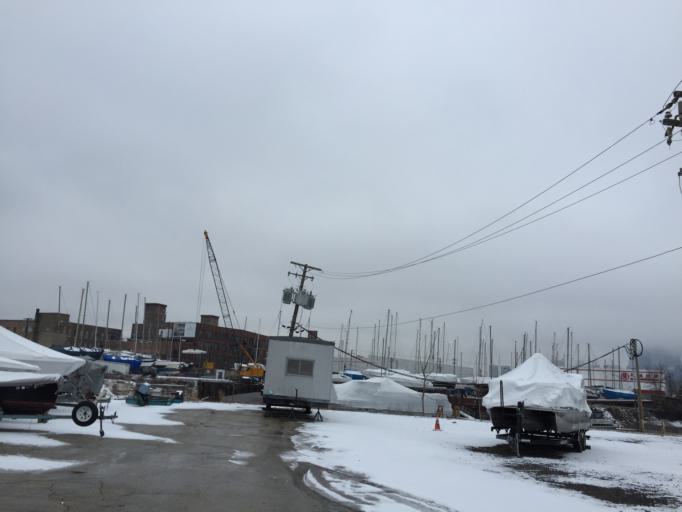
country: US
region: Illinois
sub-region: Cook County
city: Chicago
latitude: 41.8546
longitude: -87.6374
